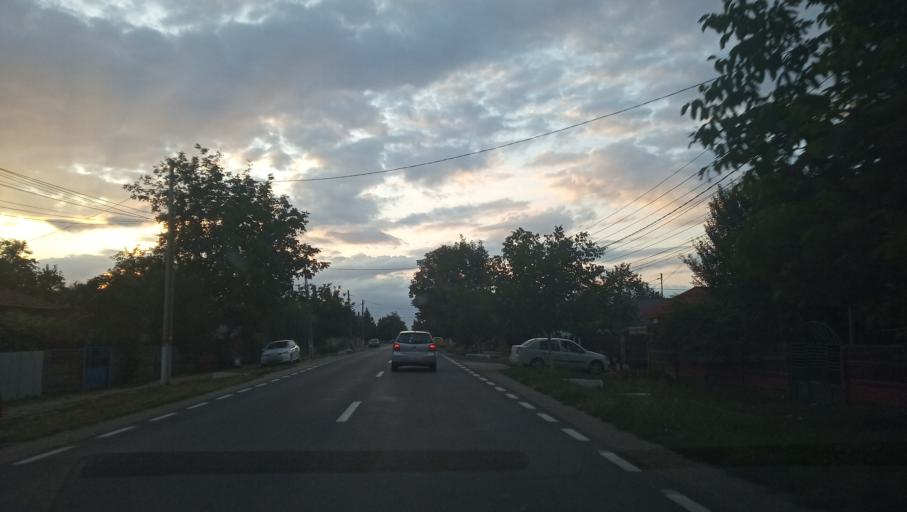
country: RO
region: Calarasi
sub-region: Oras Lehliu Gara
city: Razvani
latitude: 44.4188
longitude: 26.8825
